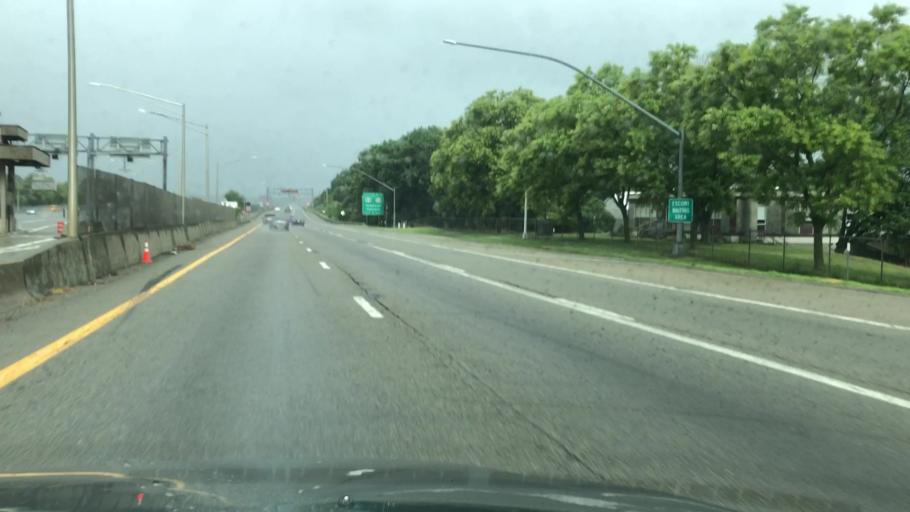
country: US
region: New York
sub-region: Dutchess County
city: Beacon
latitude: 41.5181
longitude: -73.9779
